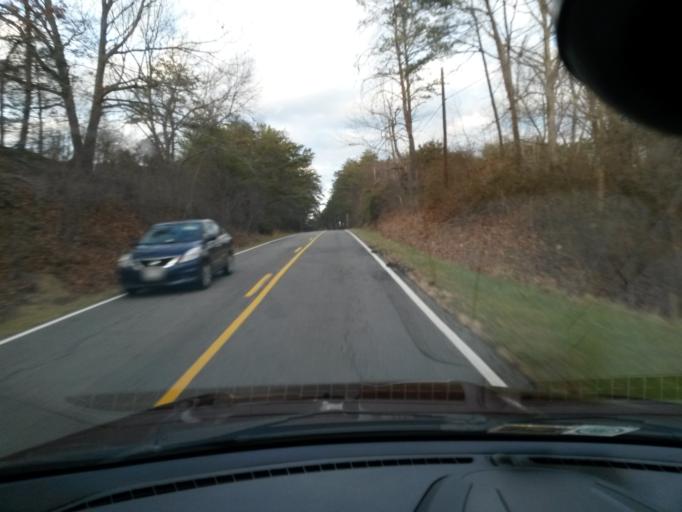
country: US
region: Virginia
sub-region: City of Covington
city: Covington
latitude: 37.7729
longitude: -80.1112
